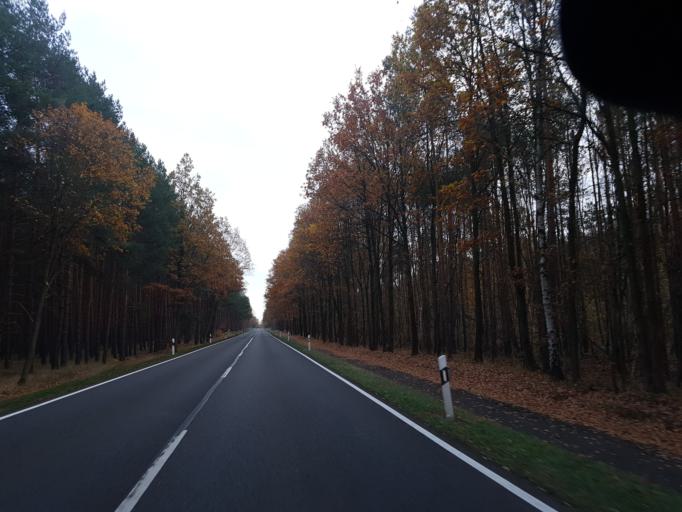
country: DE
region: Brandenburg
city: Treuenbrietzen
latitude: 52.0516
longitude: 12.9109
